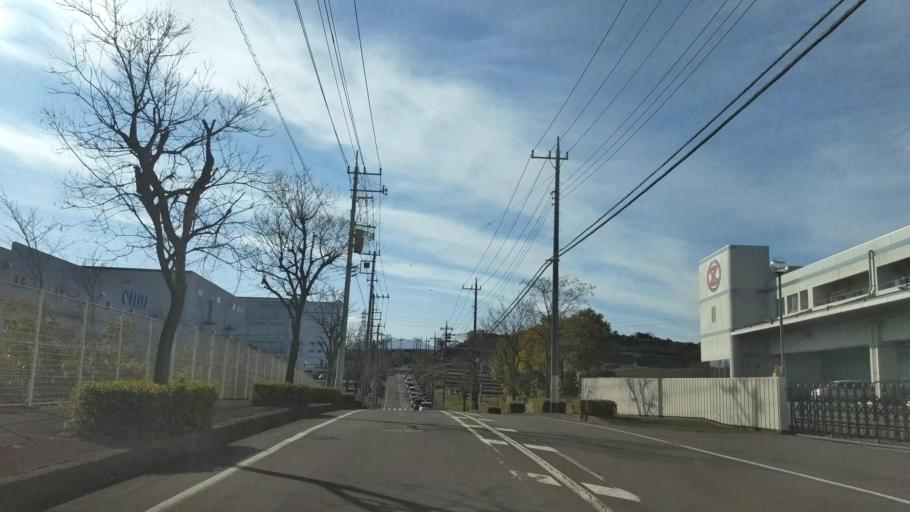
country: JP
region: Kanagawa
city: Hadano
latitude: 35.3499
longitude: 139.2312
